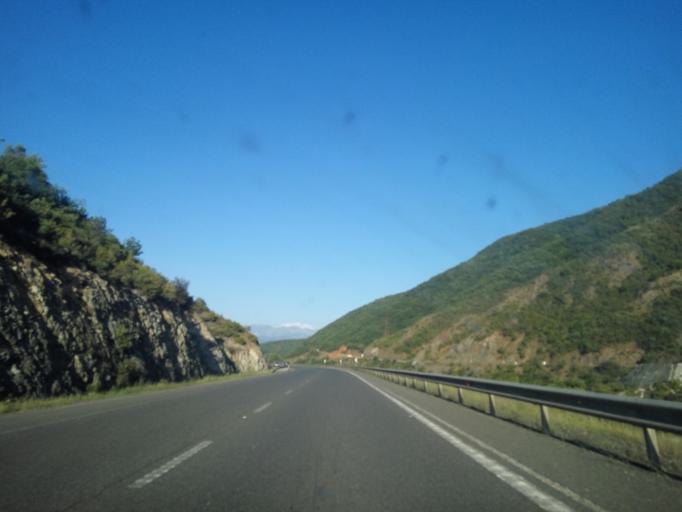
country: AL
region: Lezhe
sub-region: Rrethi i Mirdites
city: Rreshen
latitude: 41.7809
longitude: 19.8368
